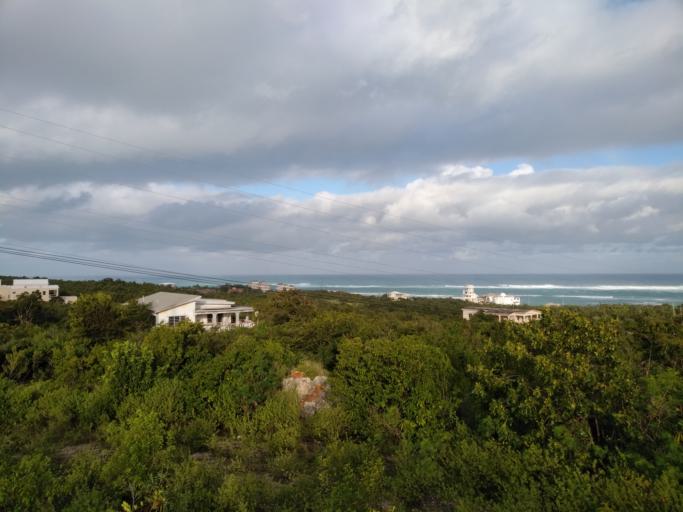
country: AI
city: Island Harbour
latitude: 18.2491
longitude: -63.0305
